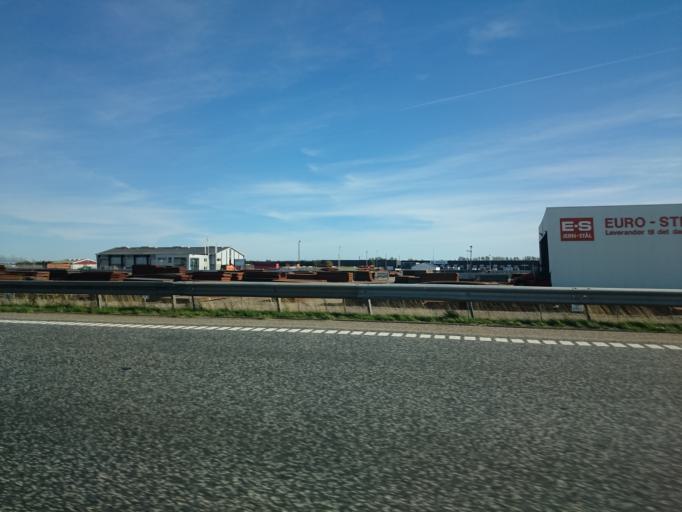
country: DK
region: Central Jutland
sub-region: Hedensted Kommune
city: Hedensted
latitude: 55.7958
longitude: 9.6720
